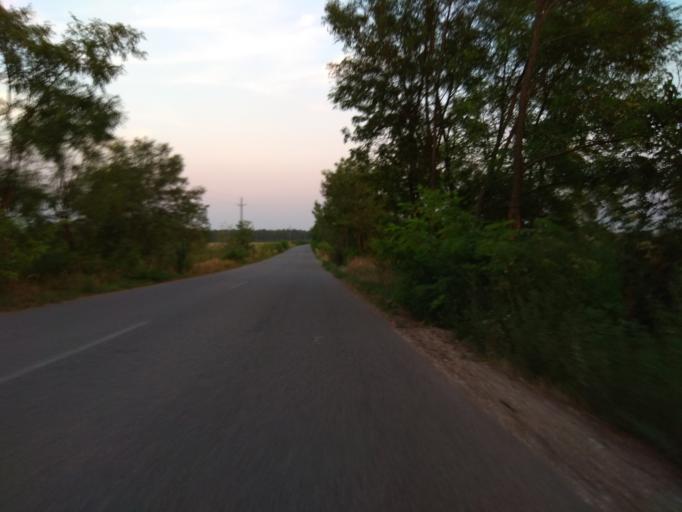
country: HU
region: Borsod-Abauj-Zemplen
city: Emod
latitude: 47.9143
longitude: 20.8485
